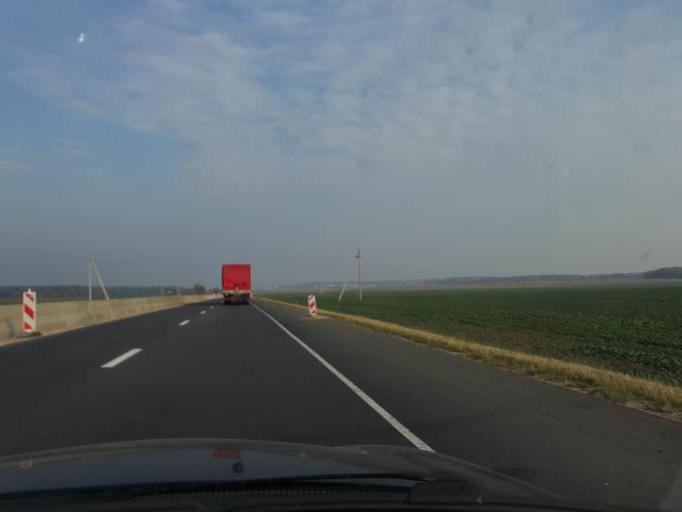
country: BY
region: Grodnenskaya
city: Shchuchin
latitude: 53.7085
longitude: 24.9316
